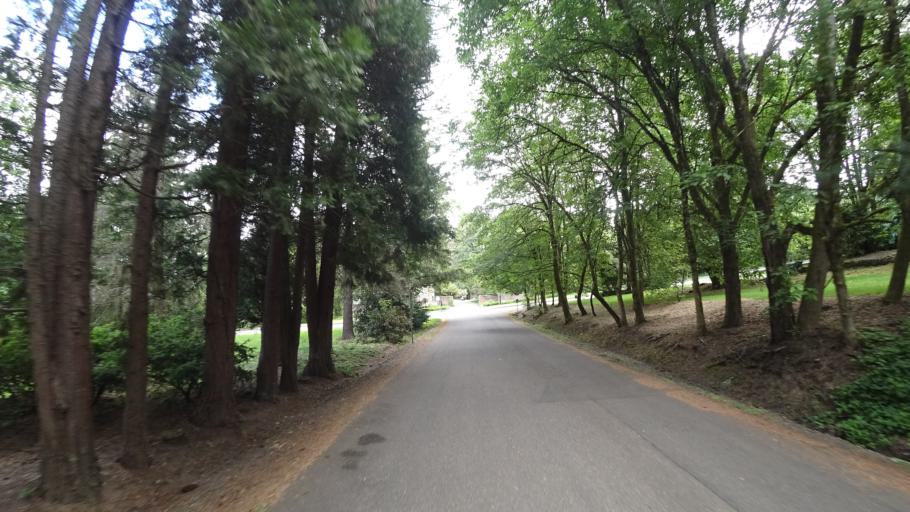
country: US
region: Oregon
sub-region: Clackamas County
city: Lake Oswego
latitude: 45.4504
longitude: -122.6733
